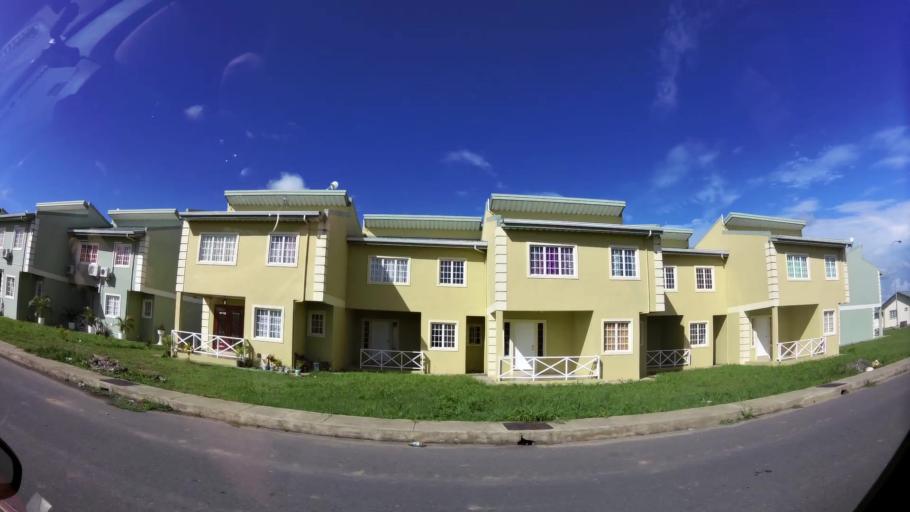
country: TT
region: Chaguanas
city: Chaguanas
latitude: 10.5328
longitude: -61.3939
